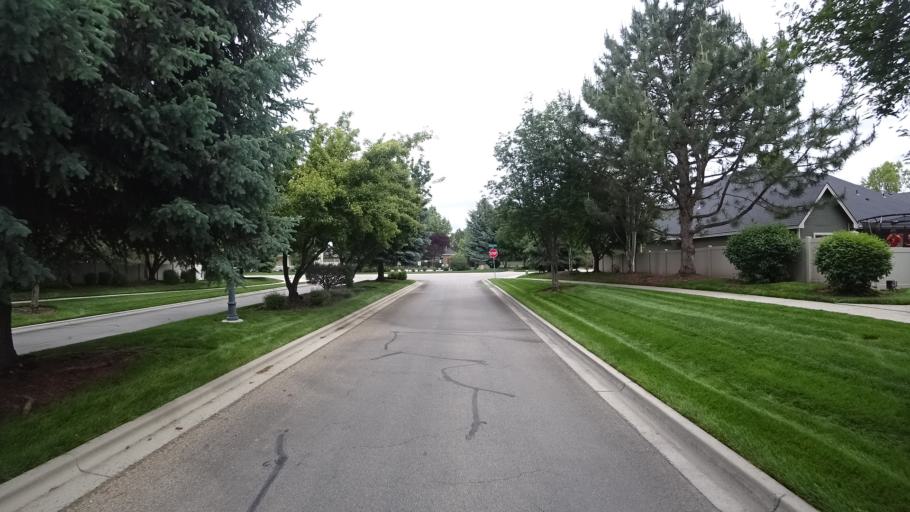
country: US
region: Idaho
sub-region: Ada County
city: Meridian
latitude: 43.6431
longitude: -116.4091
